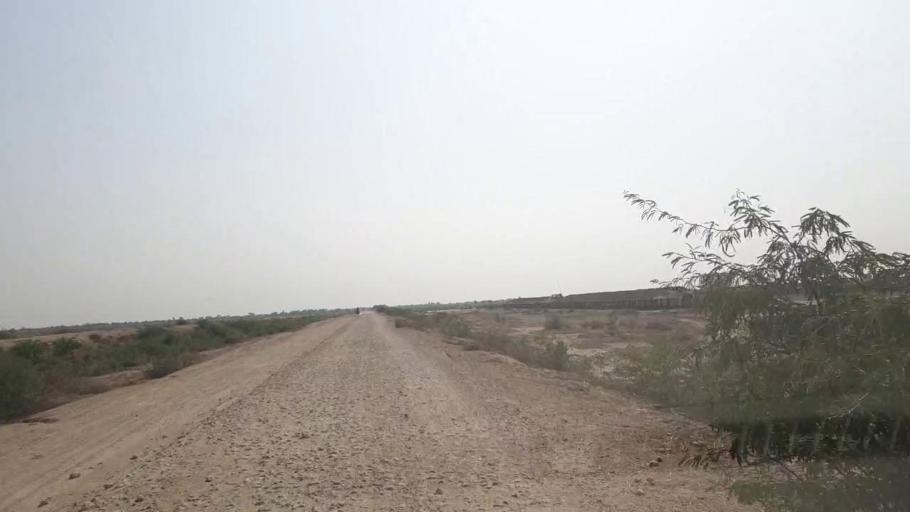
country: PK
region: Sindh
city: Kadhan
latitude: 24.4772
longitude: 68.9020
